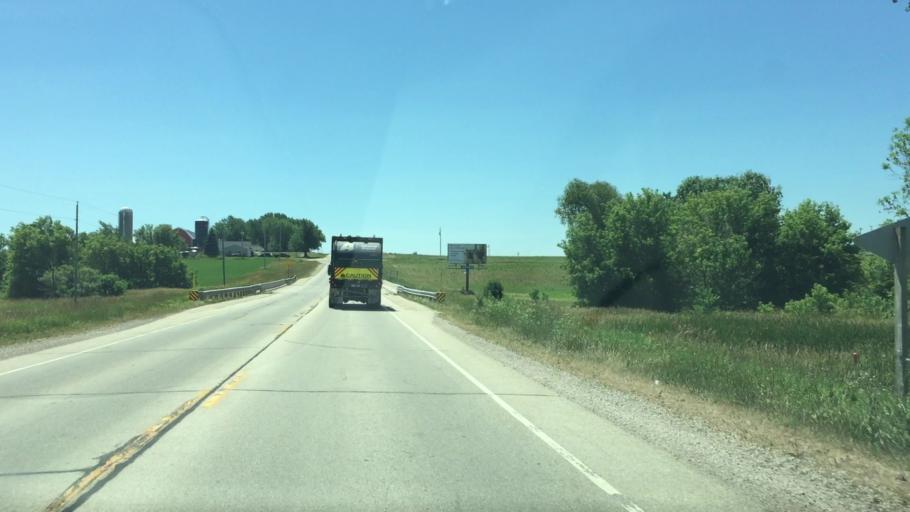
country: US
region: Wisconsin
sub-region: Calumet County
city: Chilton
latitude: 44.0613
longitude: -88.1632
